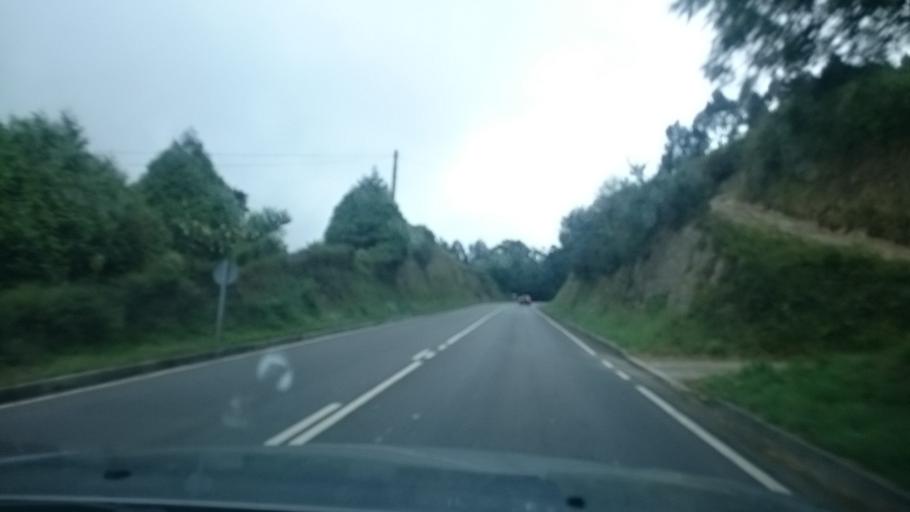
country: ES
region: Asturias
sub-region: Province of Asturias
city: Carrena
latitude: 43.4113
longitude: -4.8863
